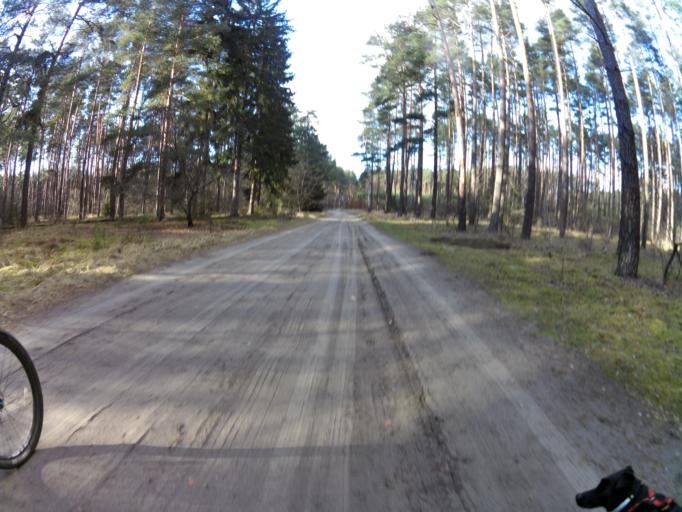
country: PL
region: West Pomeranian Voivodeship
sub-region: Powiat mysliborski
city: Debno
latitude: 52.7939
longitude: 14.7482
